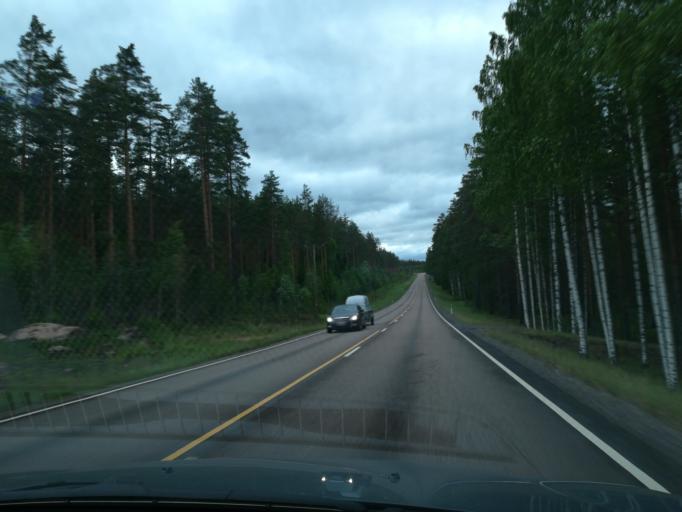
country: FI
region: Southern Savonia
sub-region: Mikkeli
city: Ristiina
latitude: 61.3394
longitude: 27.3730
